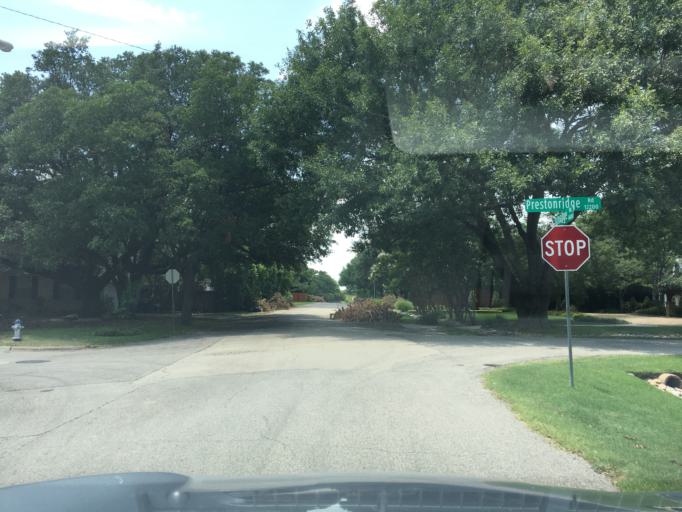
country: US
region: Texas
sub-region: Dallas County
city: Addison
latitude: 32.9153
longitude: -96.7918
